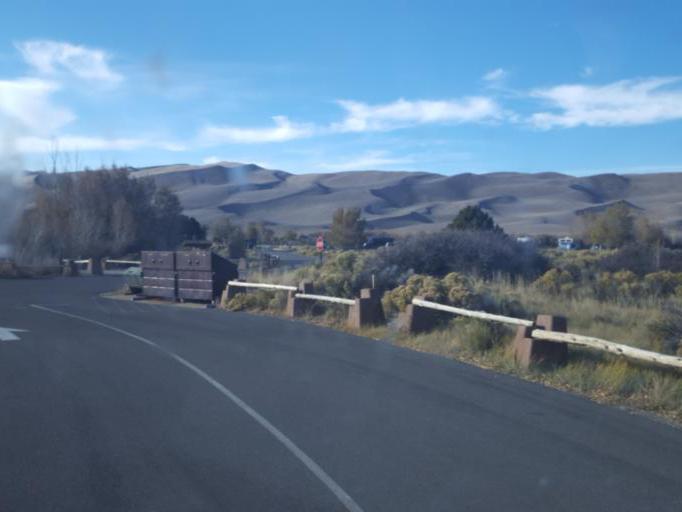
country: US
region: Colorado
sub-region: Custer County
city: Westcliffe
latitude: 37.7386
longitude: -105.5160
